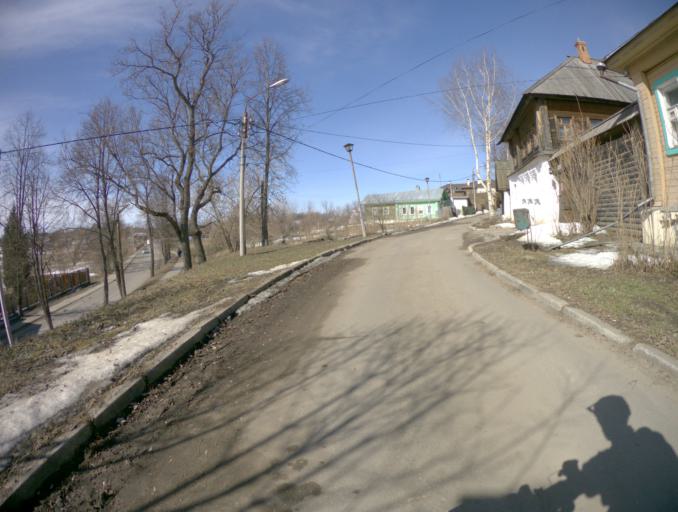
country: RU
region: Vladimir
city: Suzdal'
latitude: 56.4242
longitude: 40.4394
